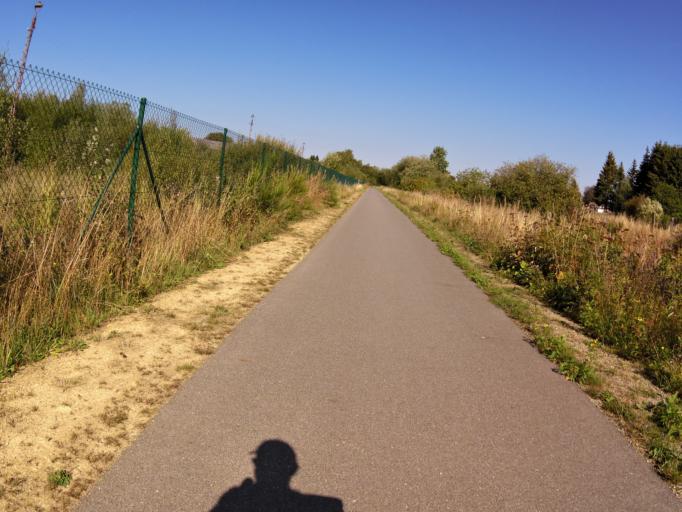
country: BE
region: Wallonia
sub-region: Province de Liege
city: Butgenbach
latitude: 50.4191
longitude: 6.1710
